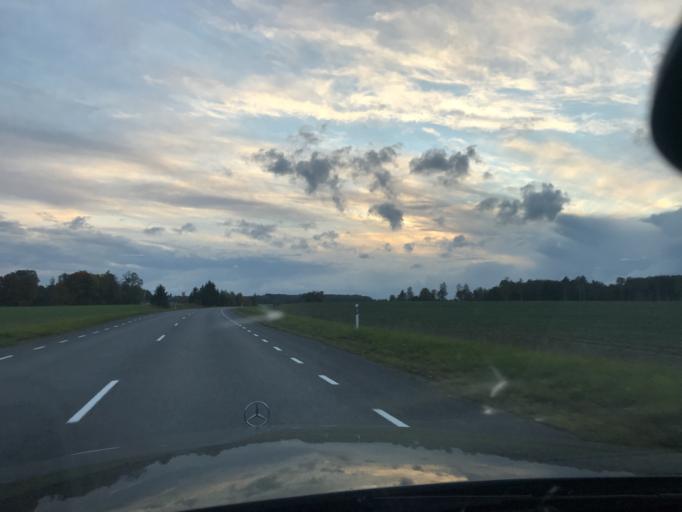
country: EE
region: Valgamaa
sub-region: Torva linn
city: Torva
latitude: 57.9798
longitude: 25.9962
